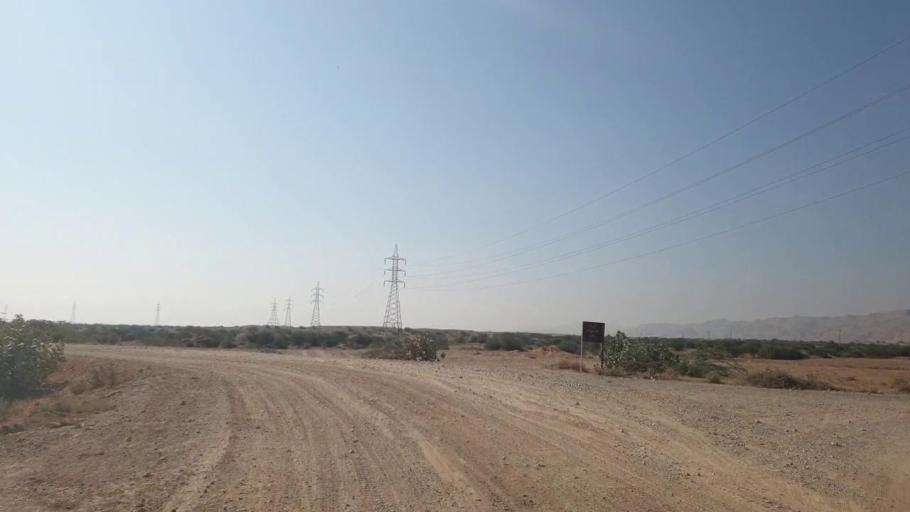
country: PK
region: Sindh
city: Gharo
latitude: 25.1479
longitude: 67.7242
